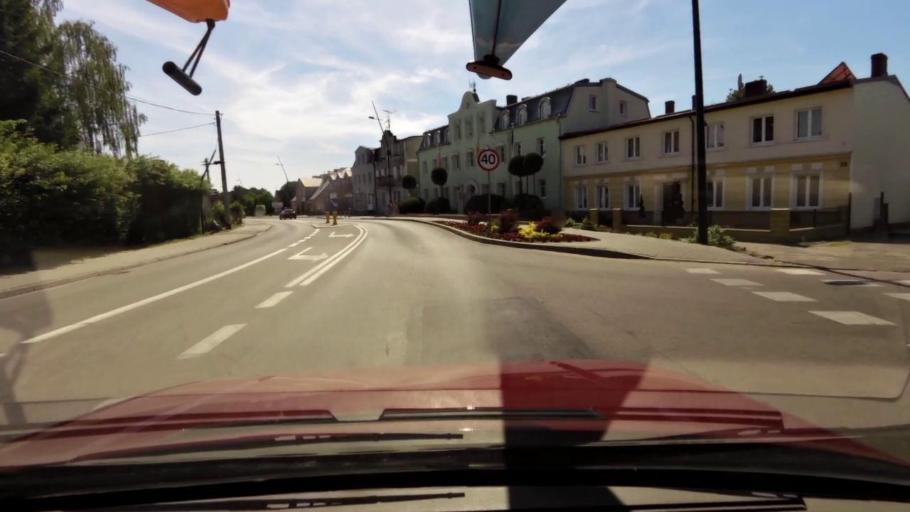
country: PL
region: Pomeranian Voivodeship
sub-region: Powiat slupski
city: Kobylnica
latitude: 54.4438
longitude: 17.0005
